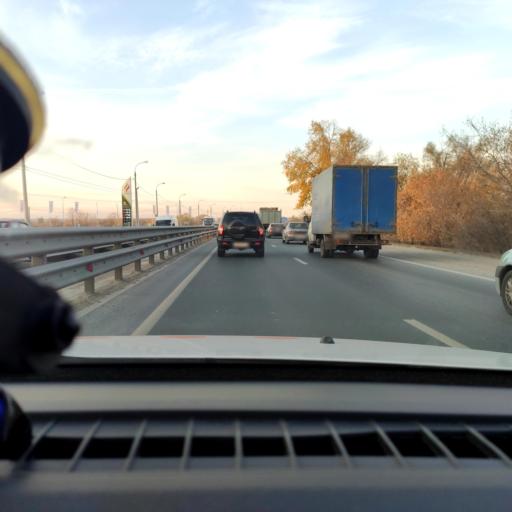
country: RU
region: Samara
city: Samara
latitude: 53.0966
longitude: 50.1574
